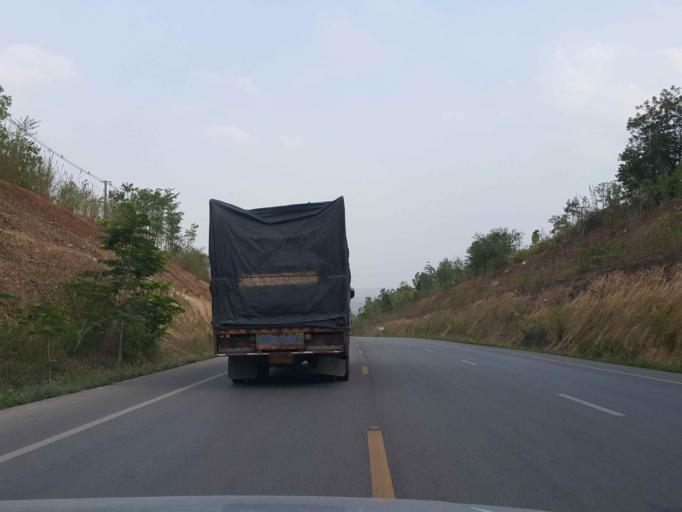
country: TH
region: Chiang Mai
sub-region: Amphoe Chiang Dao
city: Chiang Dao
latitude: 19.3577
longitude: 98.9544
